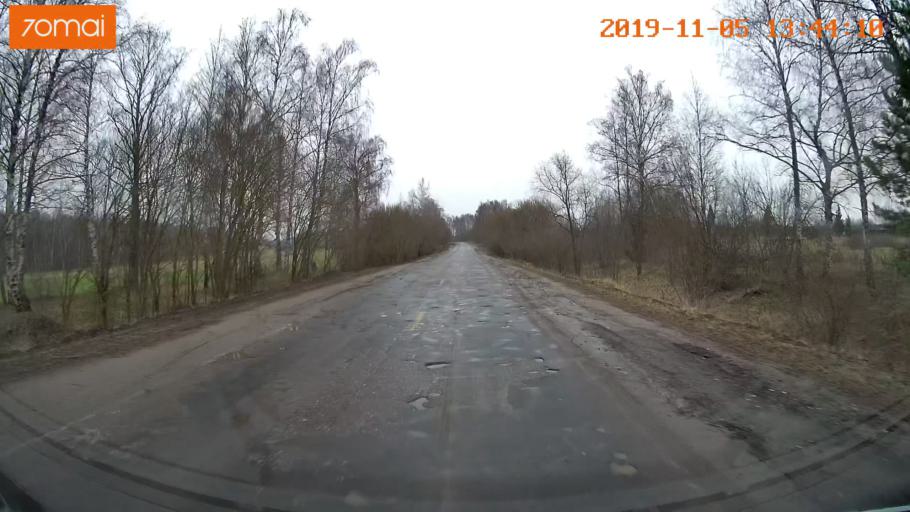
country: RU
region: Ivanovo
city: Shuya
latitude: 56.9791
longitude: 41.4087
